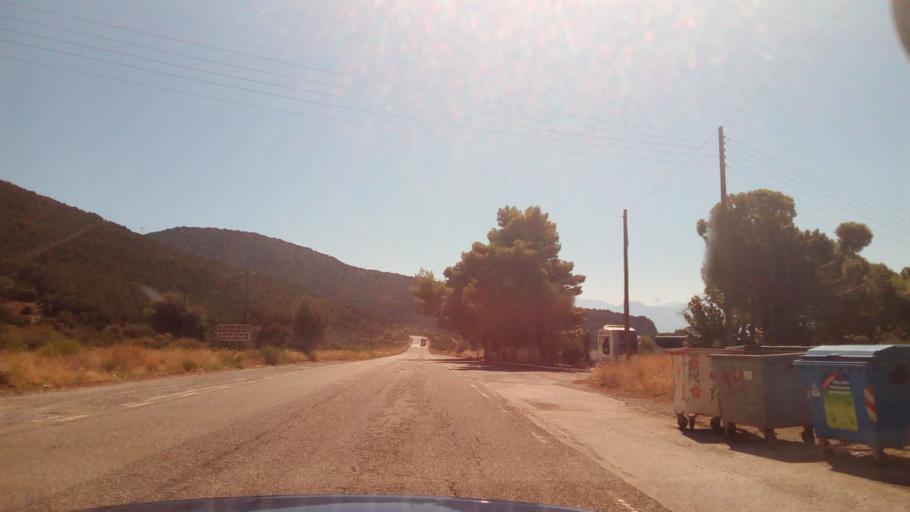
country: GR
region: West Greece
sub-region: Nomos Achaias
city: Aigio
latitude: 38.3563
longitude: 22.1398
